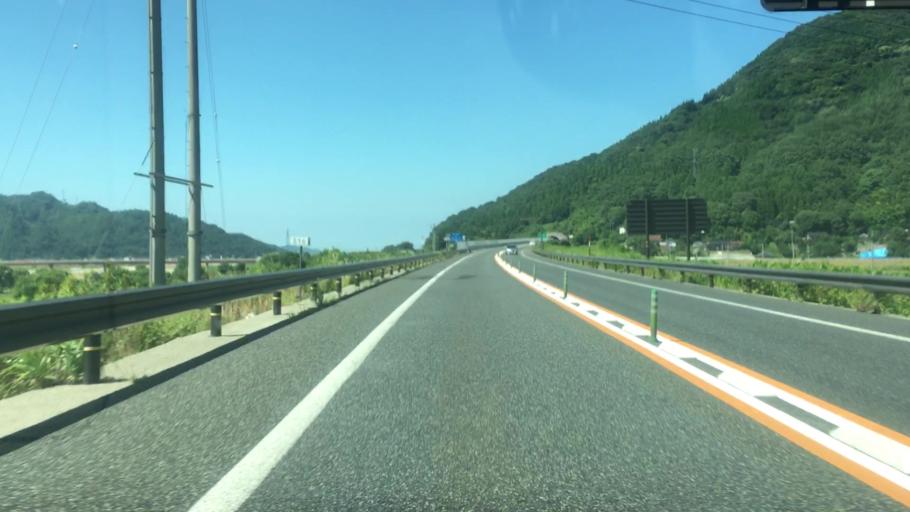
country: JP
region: Tottori
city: Tottori
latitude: 35.4028
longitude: 134.2052
